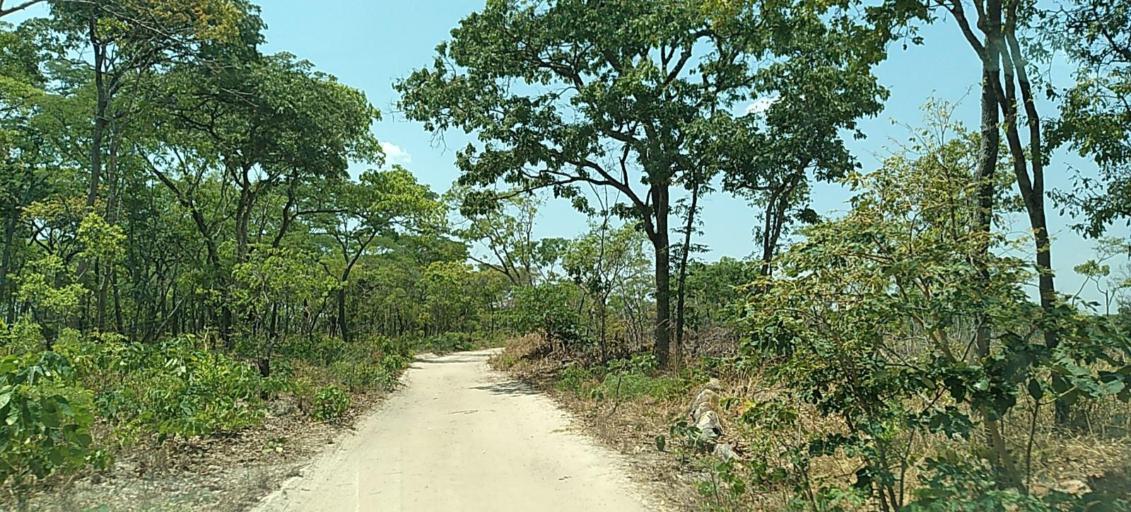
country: ZM
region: Copperbelt
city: Mpongwe
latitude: -13.6367
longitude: 28.4816
